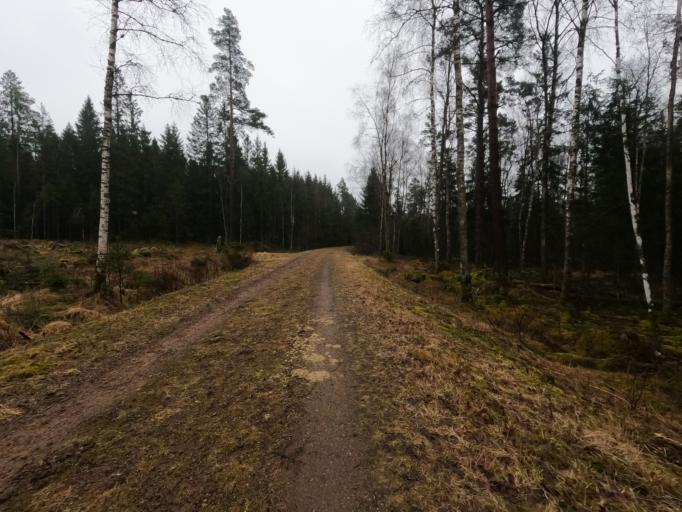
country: SE
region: Halland
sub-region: Hylte Kommun
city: Hyltebruk
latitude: 56.8026
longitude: 13.2390
